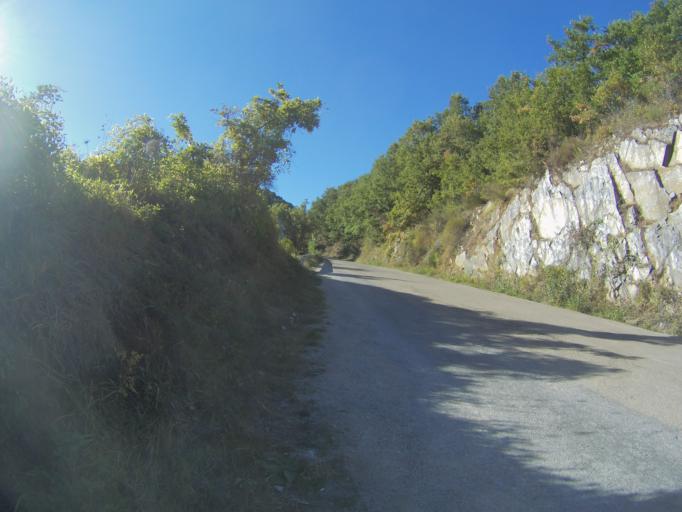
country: ES
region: Castille and Leon
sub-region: Provincia de Leon
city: Vega de Valcarce
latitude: 42.6756
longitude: -6.9982
